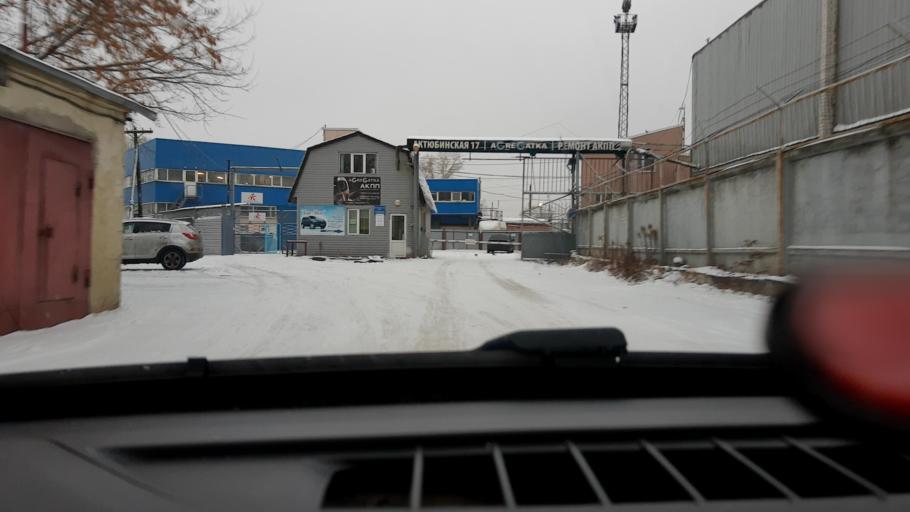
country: RU
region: Nizjnij Novgorod
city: Nizhniy Novgorod
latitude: 56.3071
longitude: 43.8899
